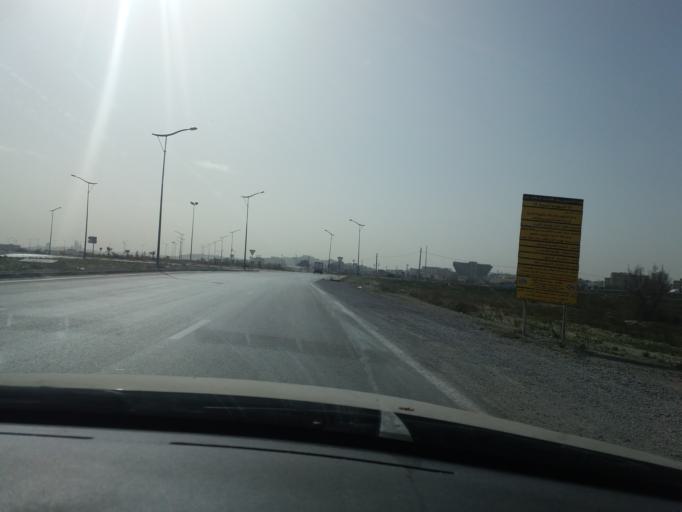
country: TN
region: Tunis
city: Tunis
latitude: 36.8107
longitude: 10.1935
